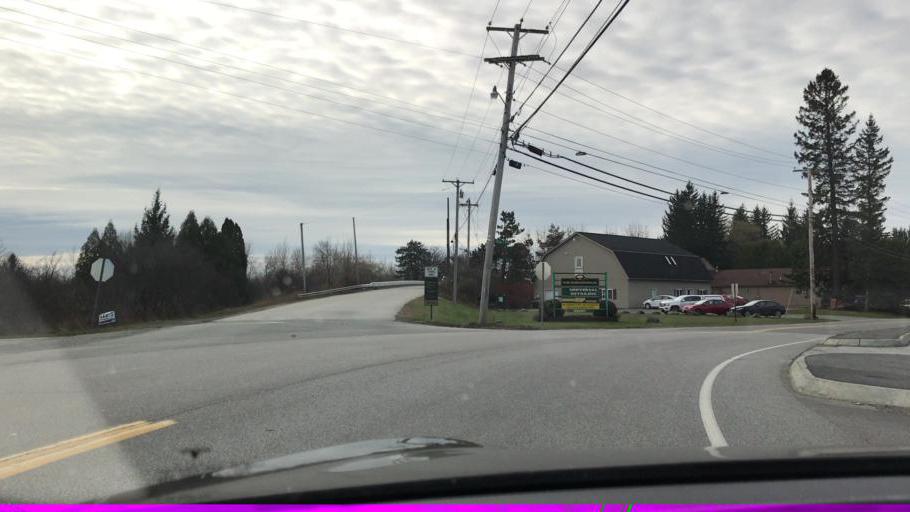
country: US
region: Maine
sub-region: Penobscot County
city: Hampden
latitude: 44.7820
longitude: -68.8165
